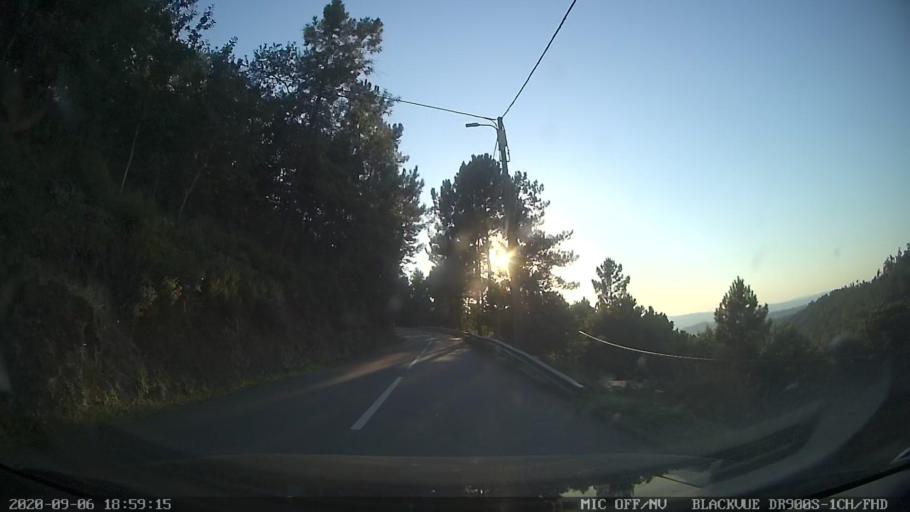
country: PT
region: Porto
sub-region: Baiao
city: Baiao
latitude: 41.2436
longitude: -7.9951
